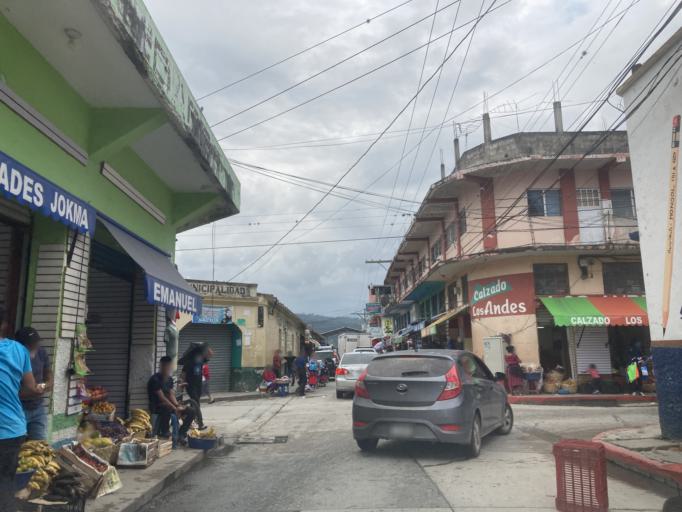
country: GT
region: Huehuetenango
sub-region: Municipio de Huehuetenango
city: Huehuetenango
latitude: 15.3217
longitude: -91.4683
